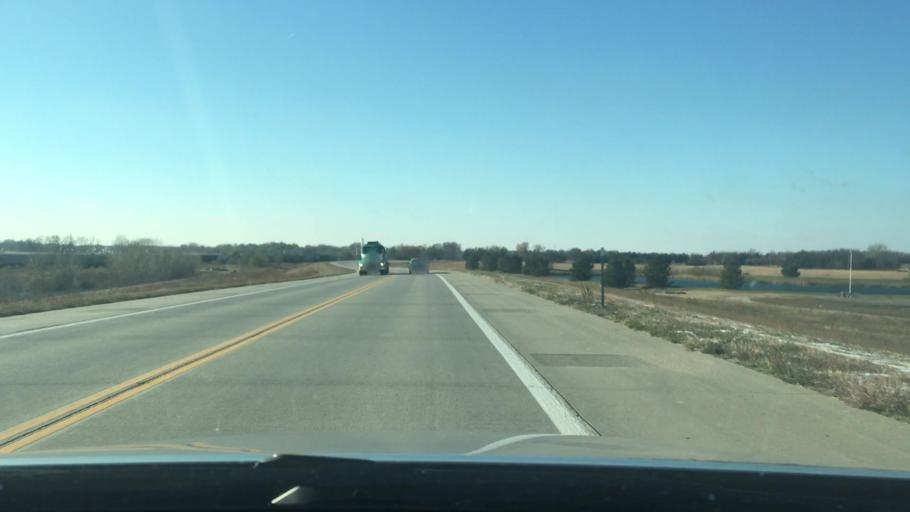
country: US
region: Kansas
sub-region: Reno County
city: Nickerson
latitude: 38.1031
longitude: -98.0162
